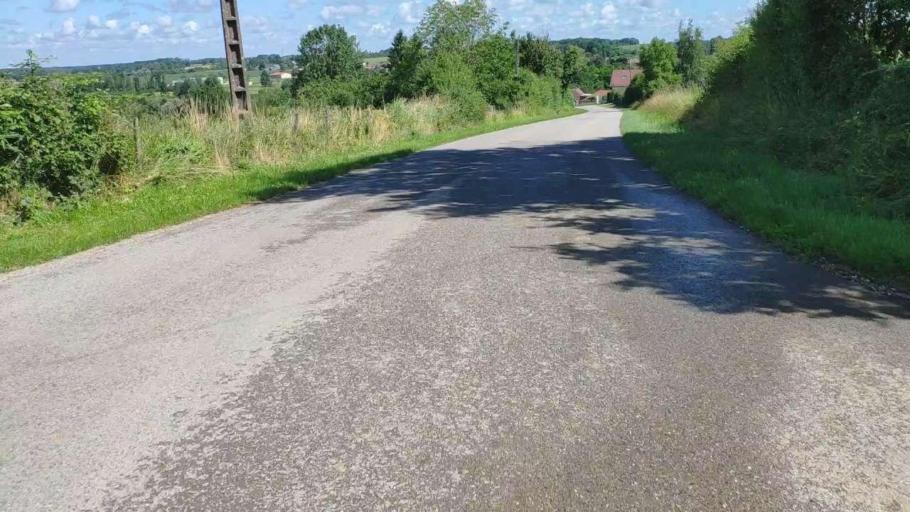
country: FR
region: Franche-Comte
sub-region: Departement du Jura
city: Bletterans
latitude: 46.8227
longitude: 5.5585
